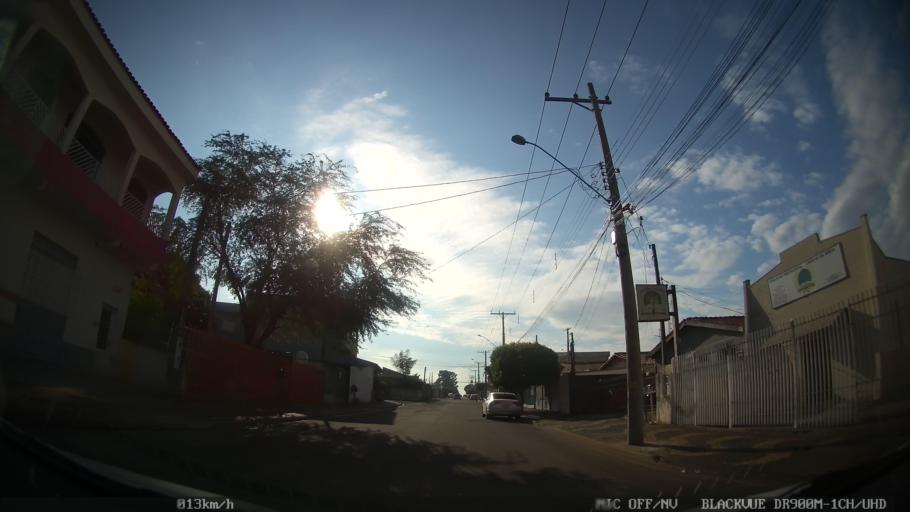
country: BR
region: Sao Paulo
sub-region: Americana
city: Americana
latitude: -22.7254
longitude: -47.3723
